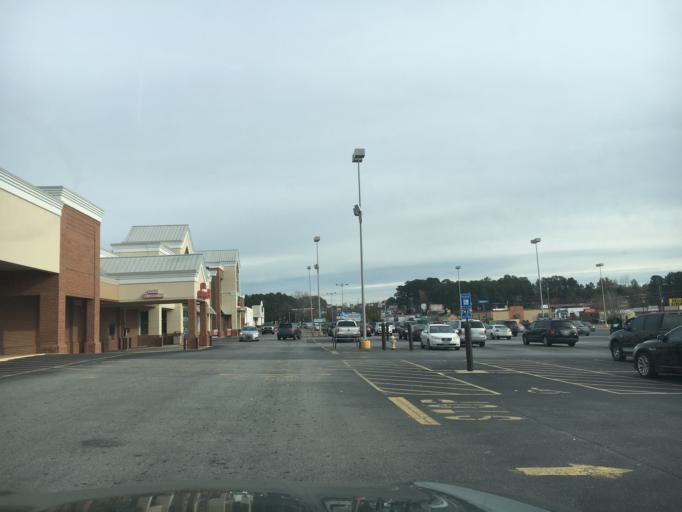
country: US
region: South Carolina
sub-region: Laurens County
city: Watts Mills
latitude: 34.4947
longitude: -81.9840
